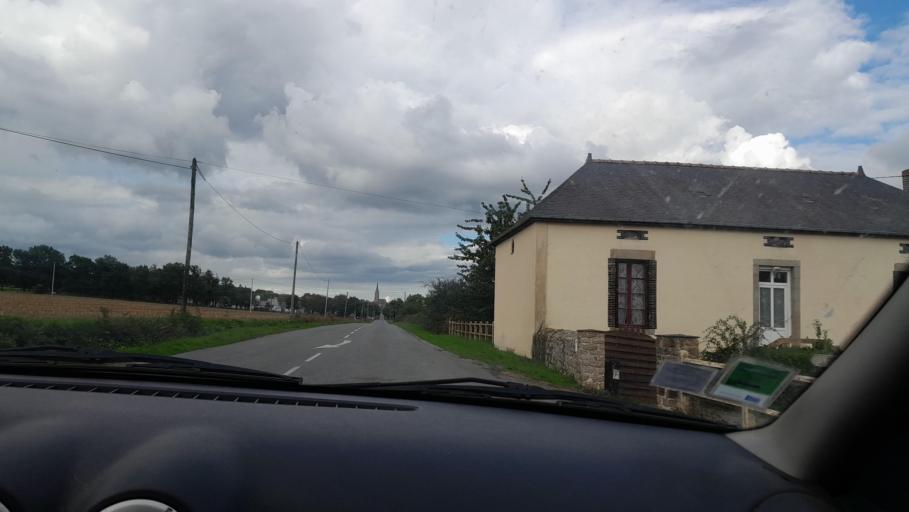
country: FR
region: Brittany
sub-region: Departement d'Ille-et-Vilaine
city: Le Pertre
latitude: 48.0166
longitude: -1.0377
